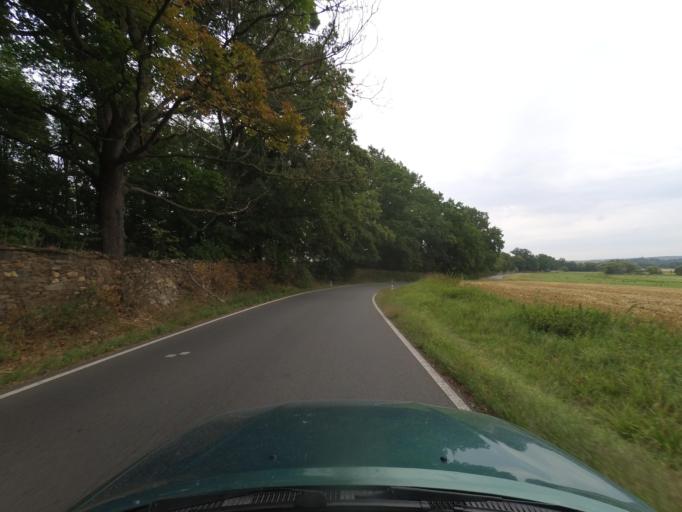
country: CZ
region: Plzensky
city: Meclov
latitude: 49.5329
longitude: 12.8965
